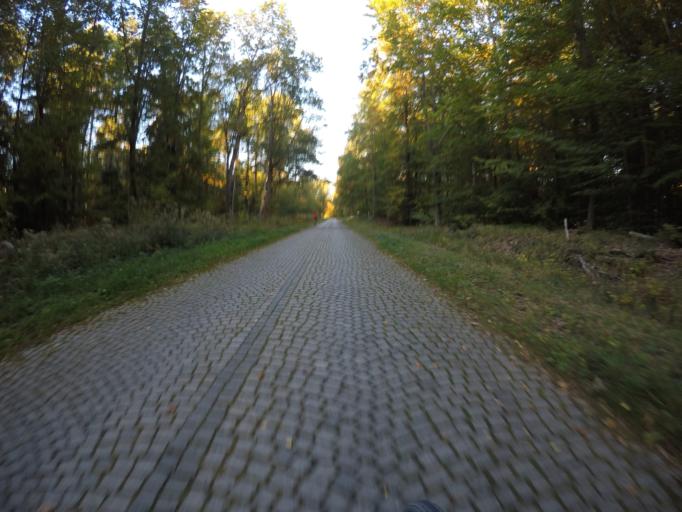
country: DE
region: Baden-Wuerttemberg
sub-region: Regierungsbezirk Stuttgart
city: Steinenbronn
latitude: 48.7136
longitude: 9.0836
